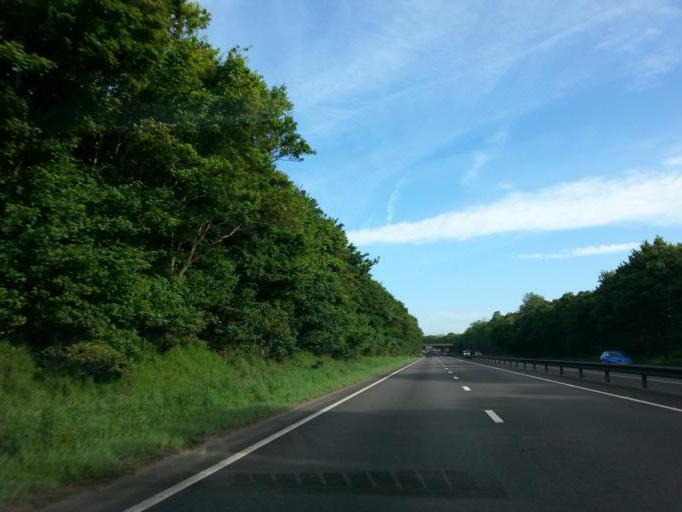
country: GB
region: England
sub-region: Nottinghamshire
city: Newark on Trent
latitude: 53.0740
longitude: -0.7692
